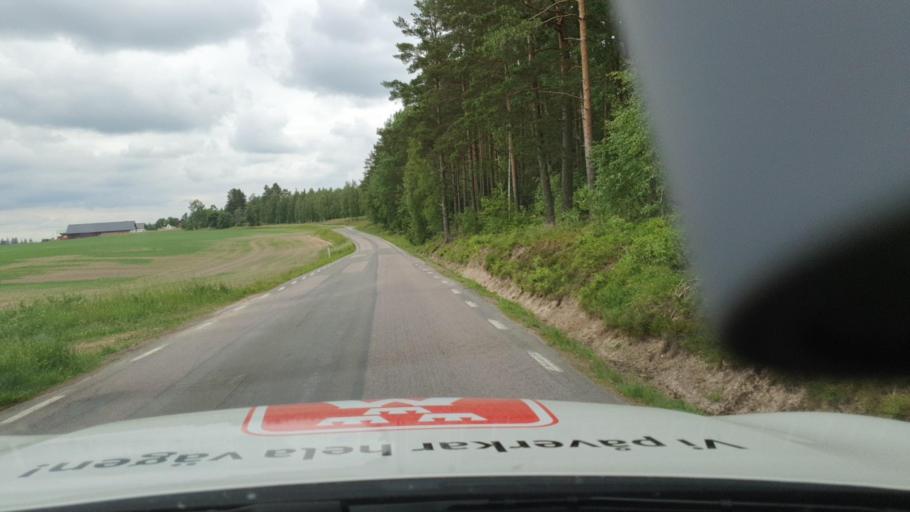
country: SE
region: Vaestra Goetaland
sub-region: Tidaholms Kommun
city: Olofstorp
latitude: 58.2698
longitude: 14.0997
